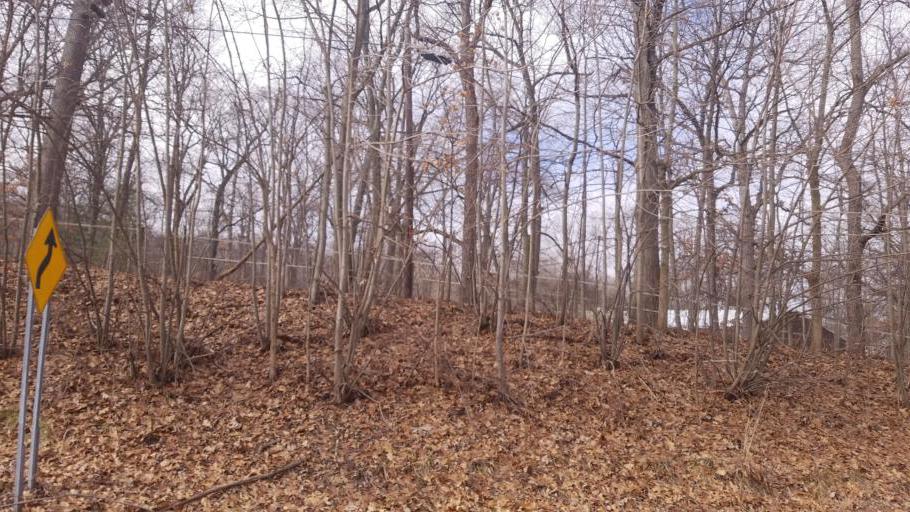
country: US
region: Ohio
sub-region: Crawford County
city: Bucyrus
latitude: 40.7518
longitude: -82.9075
